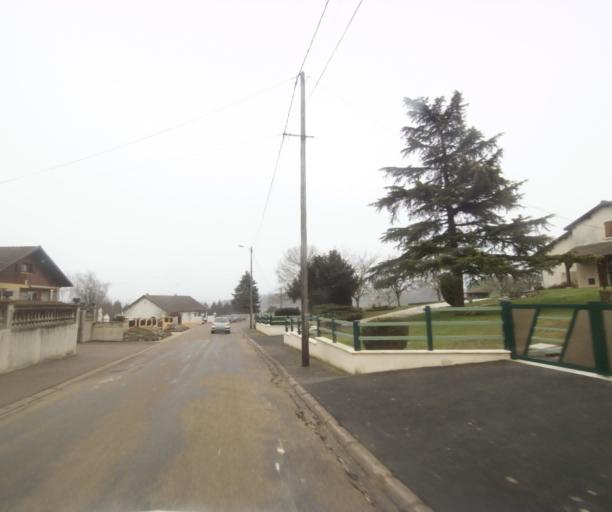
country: FR
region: Champagne-Ardenne
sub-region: Departement de la Haute-Marne
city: Bienville
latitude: 48.5322
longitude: 5.0504
